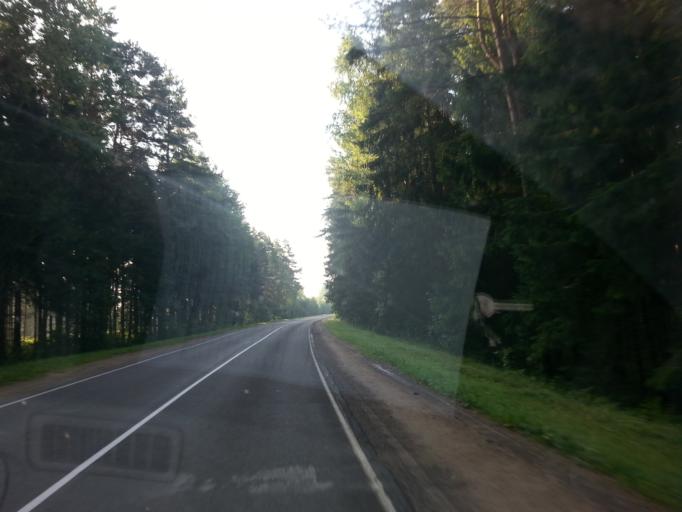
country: BY
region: Minsk
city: Myadzyel
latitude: 54.7648
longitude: 27.0967
